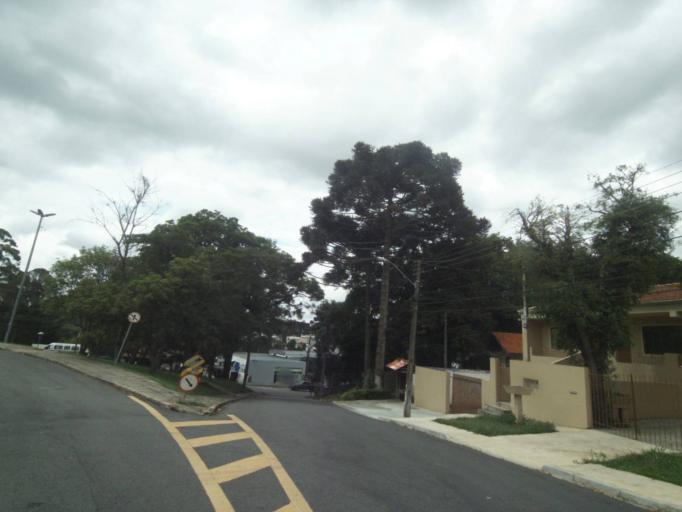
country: BR
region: Parana
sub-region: Curitiba
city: Curitiba
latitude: -25.3863
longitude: -49.2833
